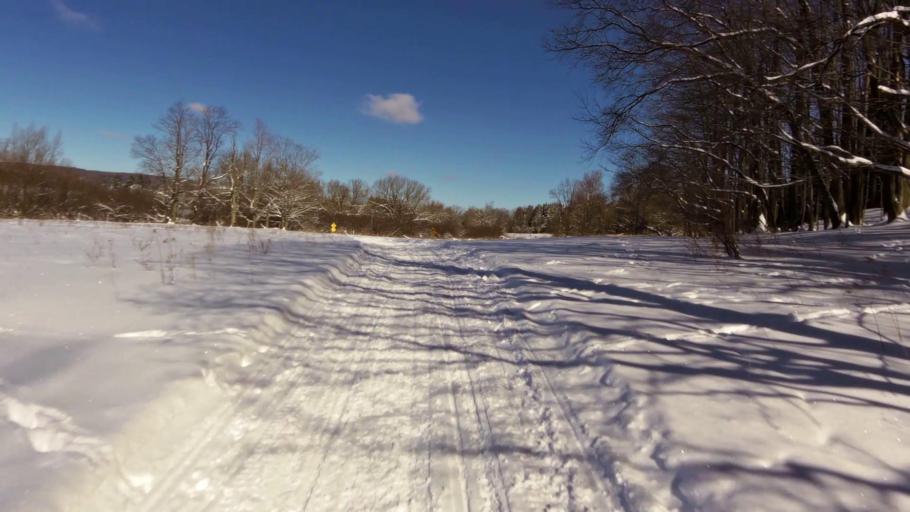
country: US
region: New York
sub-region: Chautauqua County
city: Fredonia
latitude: 42.3473
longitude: -79.1706
